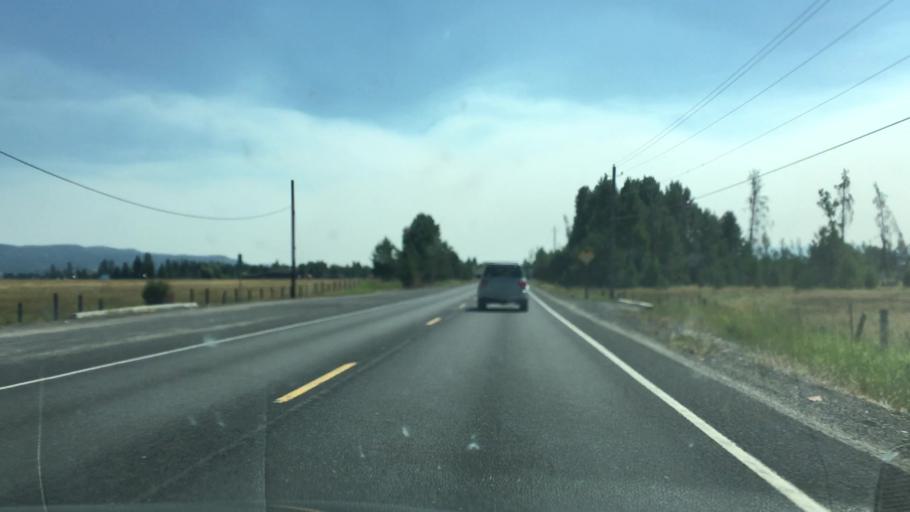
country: US
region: Idaho
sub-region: Valley County
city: McCall
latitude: 44.7410
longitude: -116.0784
